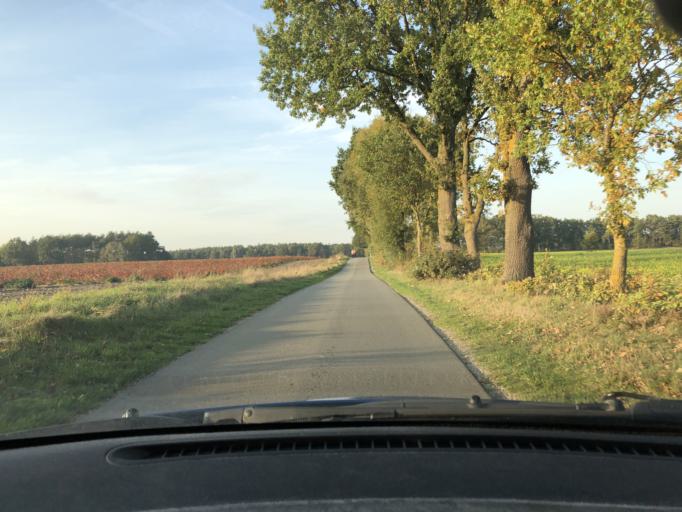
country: DE
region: Lower Saxony
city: Hitzacker
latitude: 53.1350
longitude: 11.0084
